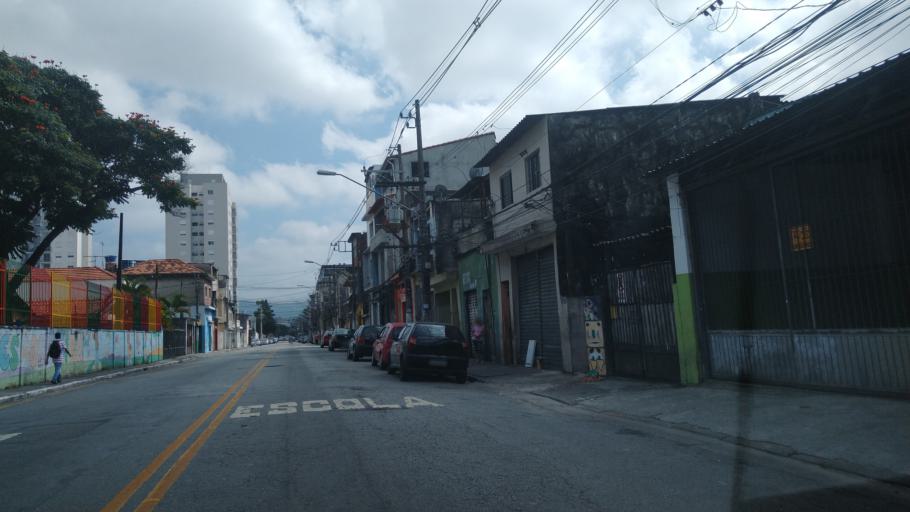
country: BR
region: Sao Paulo
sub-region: Guarulhos
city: Guarulhos
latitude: -23.4795
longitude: -46.5724
